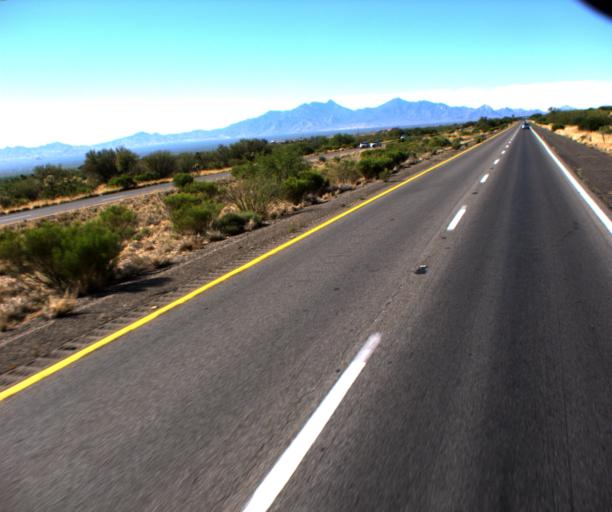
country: US
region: Arizona
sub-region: Pima County
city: Sahuarita
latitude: 31.9705
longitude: -110.9896
